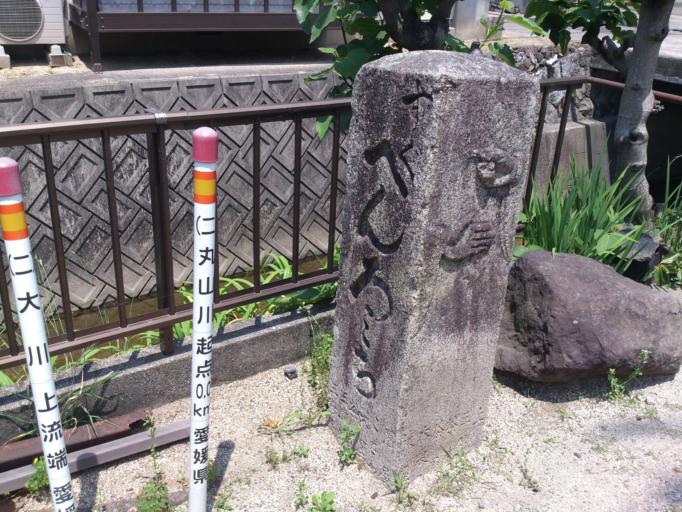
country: JP
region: Ehime
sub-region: Shikoku-chuo Shi
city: Matsuyama
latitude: 33.8535
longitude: 132.7758
